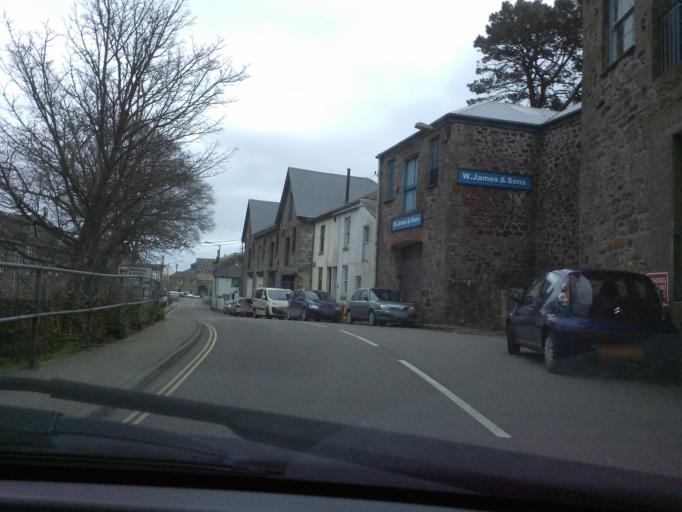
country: GB
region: England
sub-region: Cornwall
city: Penzance
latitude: 50.1074
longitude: -5.5523
